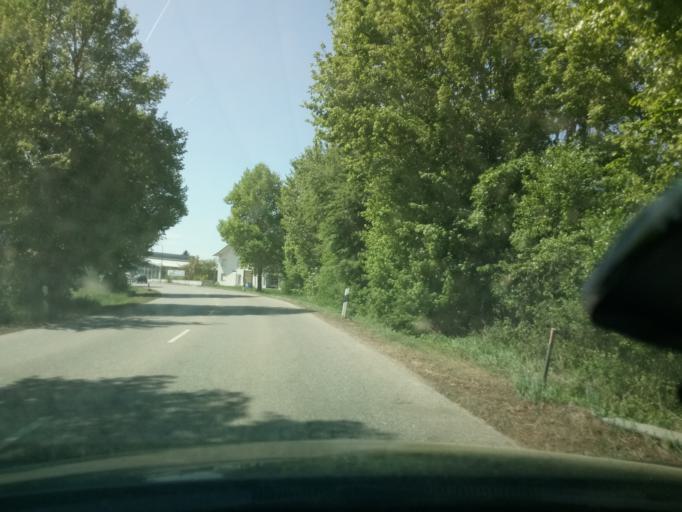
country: DE
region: Bavaria
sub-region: Upper Bavaria
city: Ampfing
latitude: 48.2500
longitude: 12.4127
